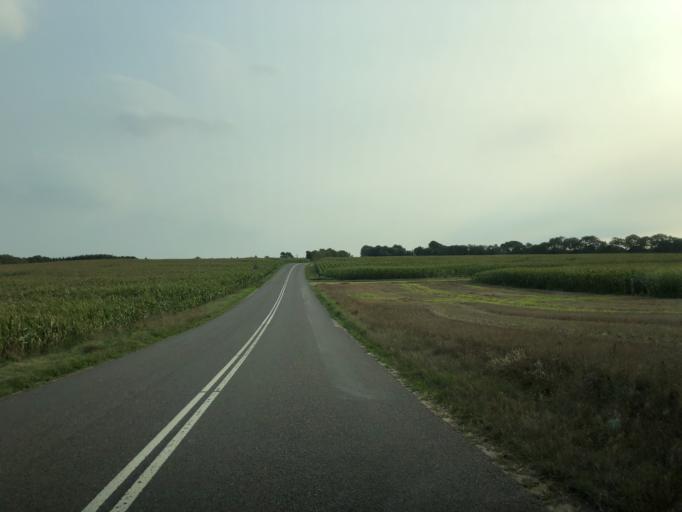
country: DK
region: Central Jutland
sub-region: Ringkobing-Skjern Kommune
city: Videbaek
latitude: 56.0774
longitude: 8.7049
